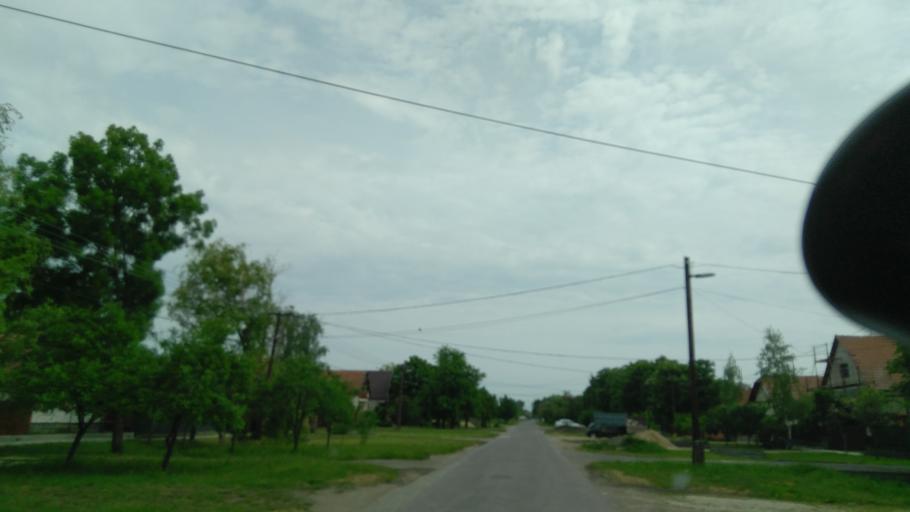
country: HU
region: Bekes
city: Szeghalom
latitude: 47.0182
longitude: 21.1672
